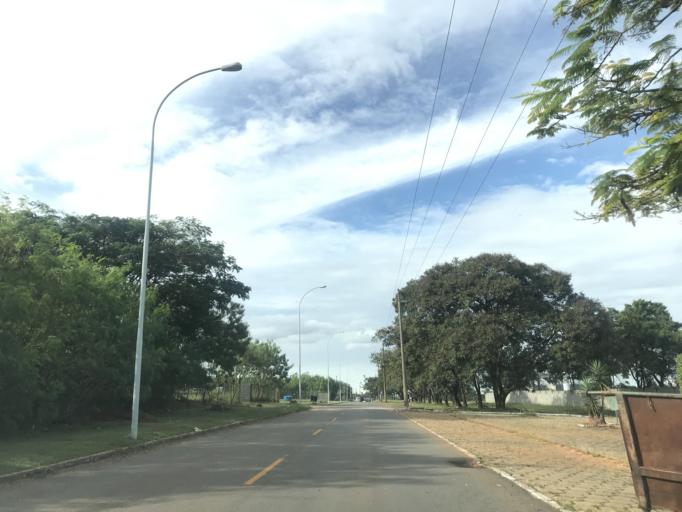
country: BR
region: Federal District
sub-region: Brasilia
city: Brasilia
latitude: -15.8141
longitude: -47.8849
